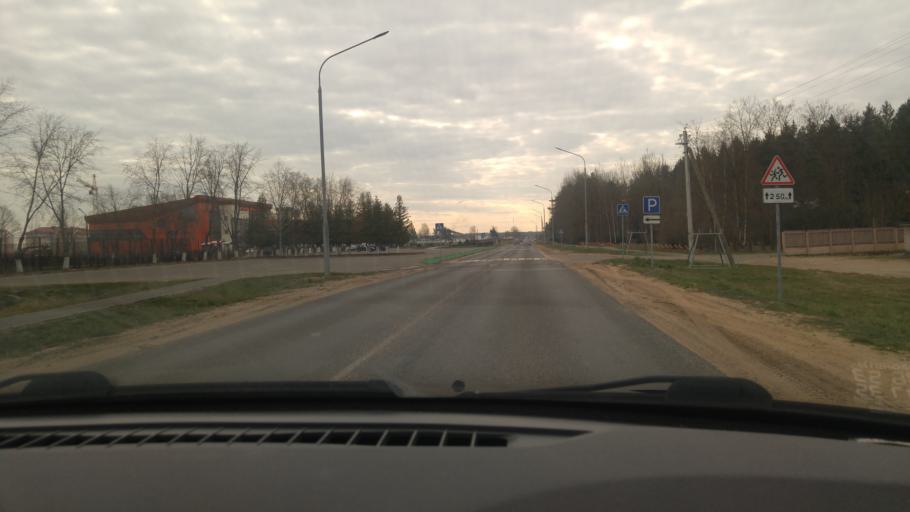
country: BY
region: Minsk
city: Chervyen'
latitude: 53.7005
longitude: 28.4151
